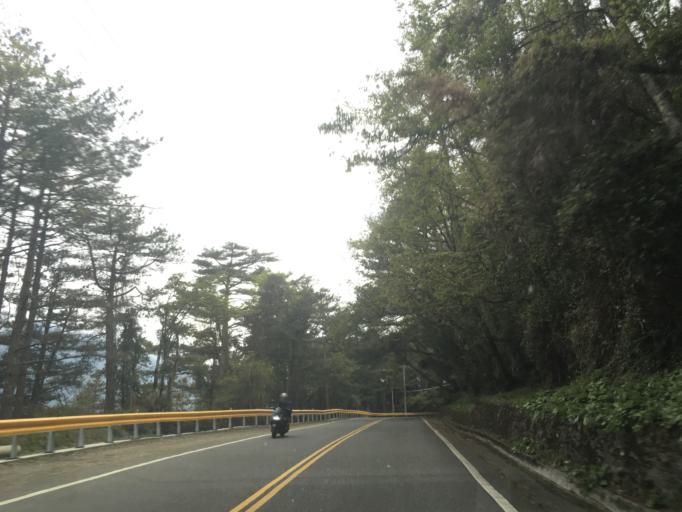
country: TW
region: Taiwan
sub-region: Hualien
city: Hualian
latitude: 24.1836
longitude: 121.3268
